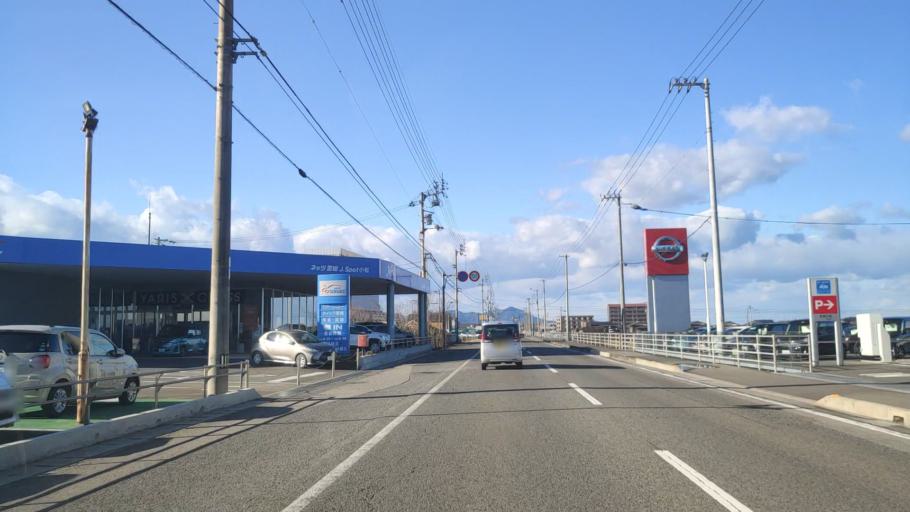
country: JP
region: Ehime
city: Saijo
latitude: 33.9109
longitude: 133.1106
